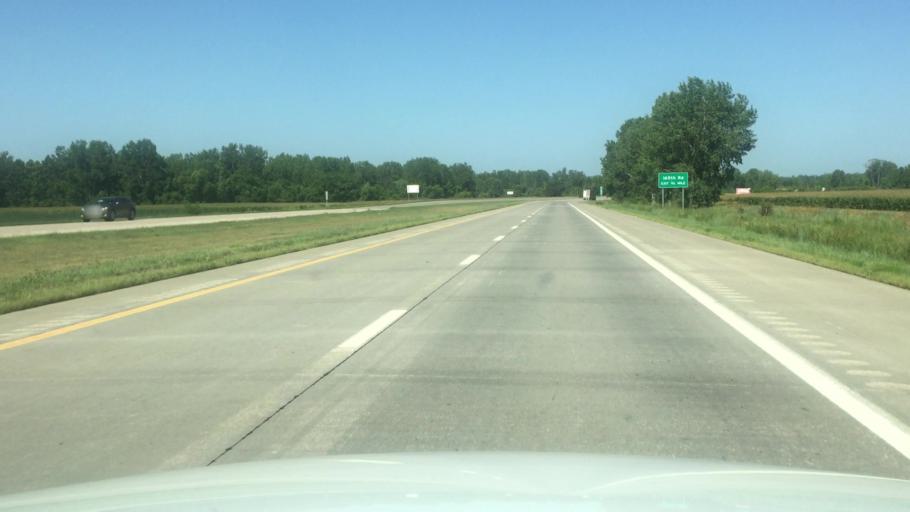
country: US
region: Kansas
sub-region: Doniphan County
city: Elwood
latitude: 39.7406
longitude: -94.9097
